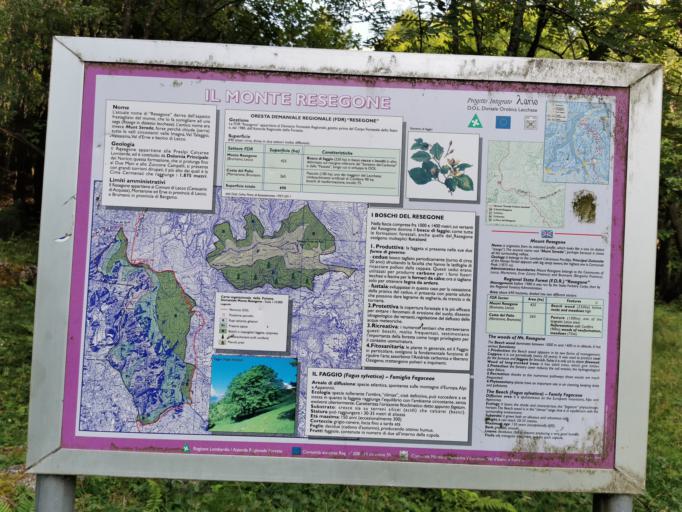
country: IT
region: Lombardy
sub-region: Provincia di Lecco
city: Morterone
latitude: 45.8662
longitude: 9.4710
